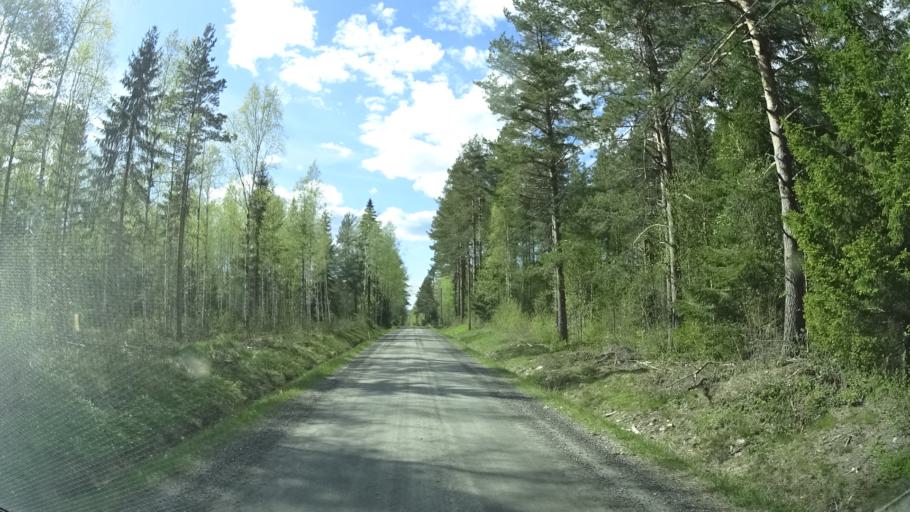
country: SE
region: OErebro
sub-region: Nora Kommun
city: As
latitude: 59.4390
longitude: 14.8512
